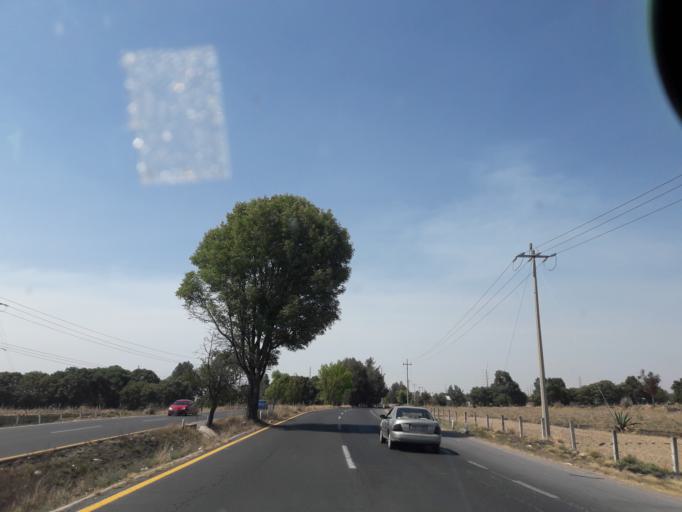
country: MX
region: Tlaxcala
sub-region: Santa Cruz Quilehtla
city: Ayometitla
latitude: 19.1967
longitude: -98.1951
